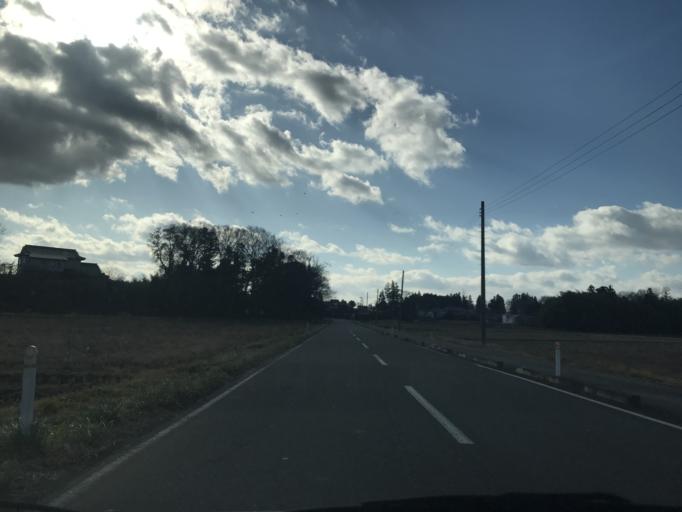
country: JP
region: Iwate
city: Ichinoseki
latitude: 38.7630
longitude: 141.0592
